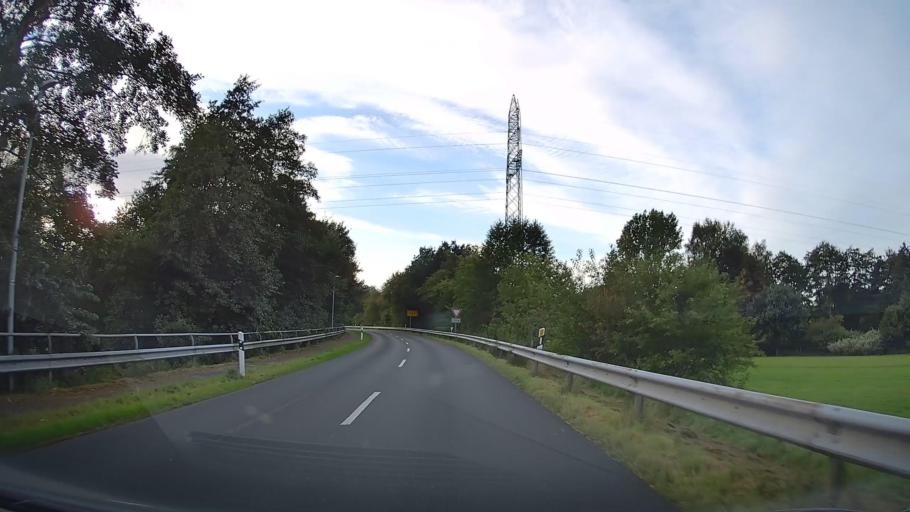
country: DE
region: Lower Saxony
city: Sottrum
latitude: 53.1024
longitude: 9.2354
